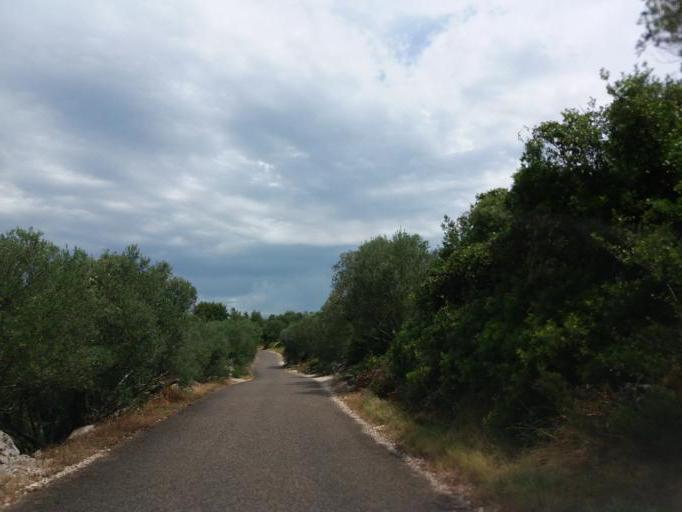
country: HR
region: Zadarska
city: Sali
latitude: 43.9326
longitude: 15.1389
